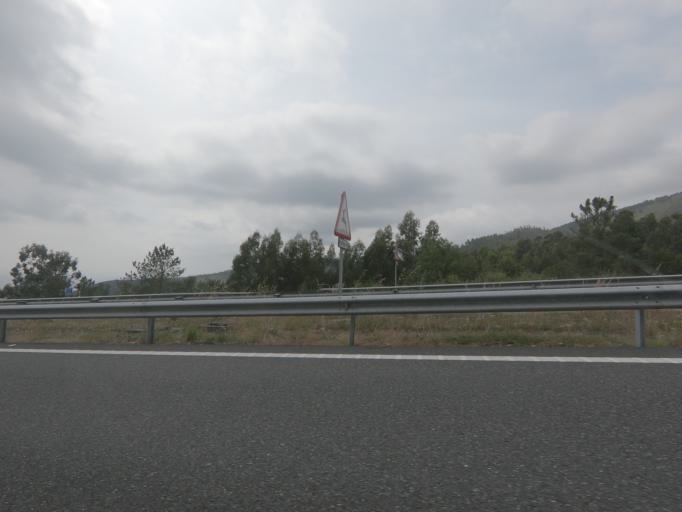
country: ES
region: Galicia
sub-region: Provincia de Pontevedra
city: Covelo
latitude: 42.1704
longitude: -8.3782
